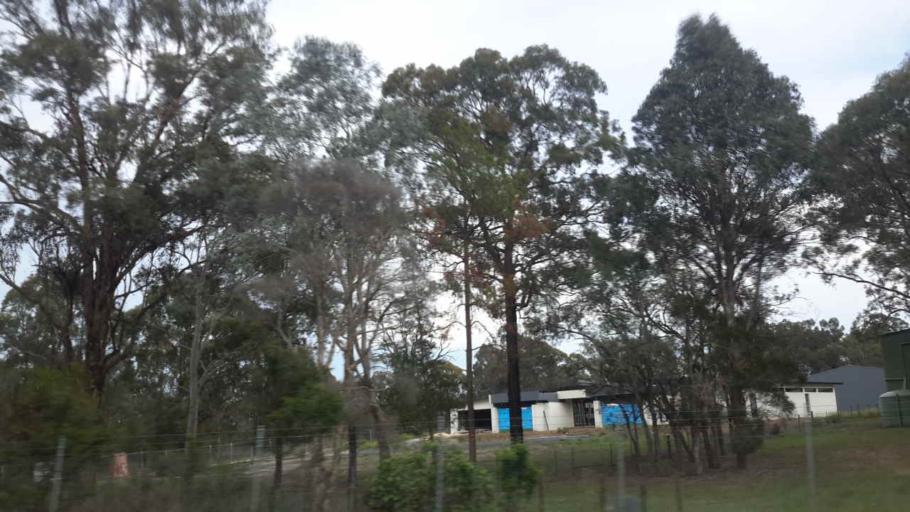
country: AU
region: New South Wales
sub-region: Penrith Municipality
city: Werrington Downs
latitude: -33.6945
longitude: 150.7277
